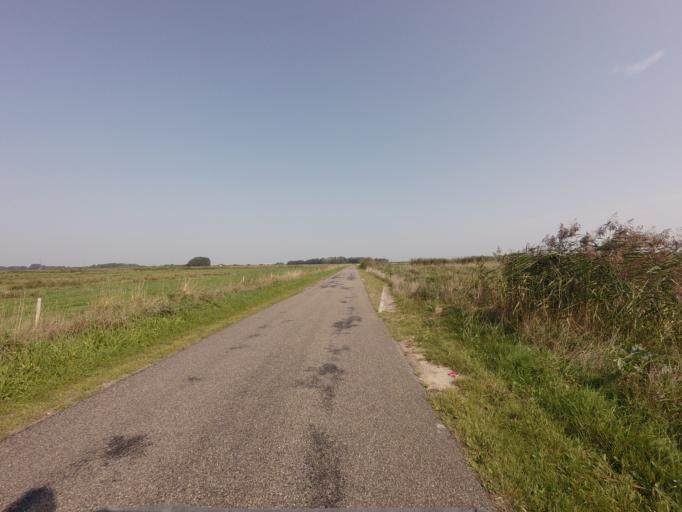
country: NL
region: Groningen
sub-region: Gemeente Groningen
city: Groningen
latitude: 53.1464
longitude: 6.5290
